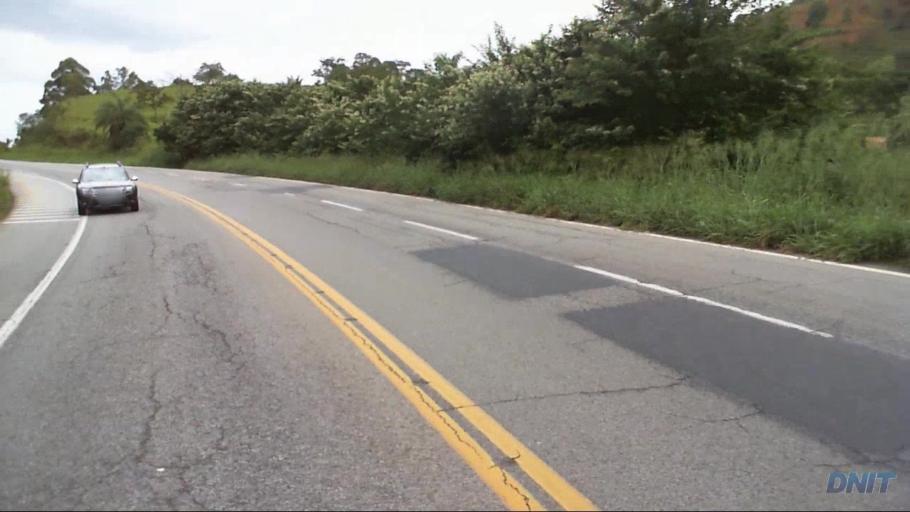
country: BR
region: Minas Gerais
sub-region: Barao De Cocais
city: Barao de Cocais
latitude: -19.8271
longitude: -43.3838
